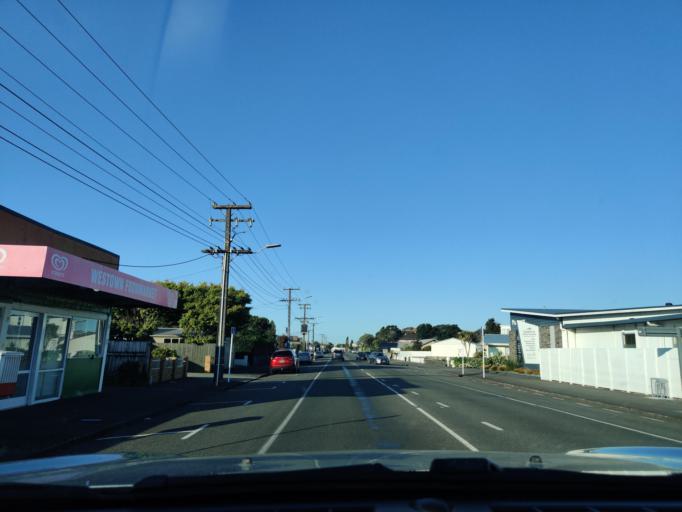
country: NZ
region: Taranaki
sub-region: New Plymouth District
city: New Plymouth
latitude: -39.0738
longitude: 174.0589
